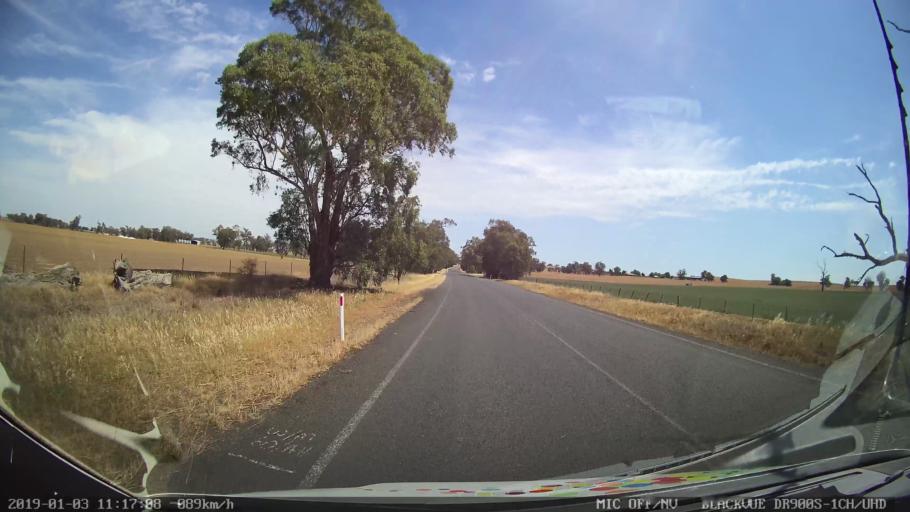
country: AU
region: New South Wales
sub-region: Young
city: Young
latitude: -34.1427
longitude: 148.2673
